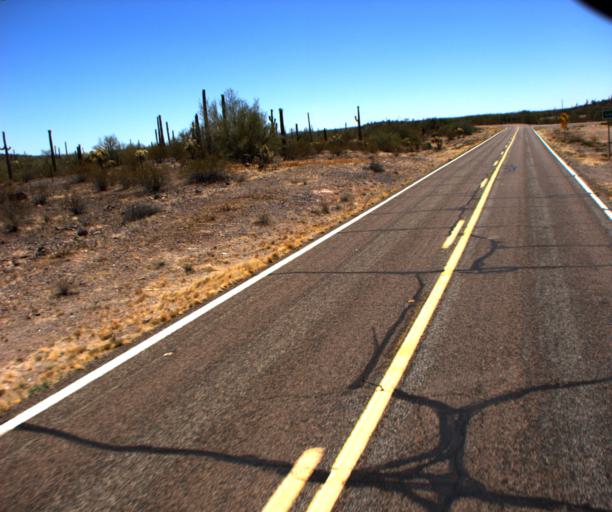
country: US
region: Arizona
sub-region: Pima County
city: Ajo
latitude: 32.2223
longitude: -112.6893
